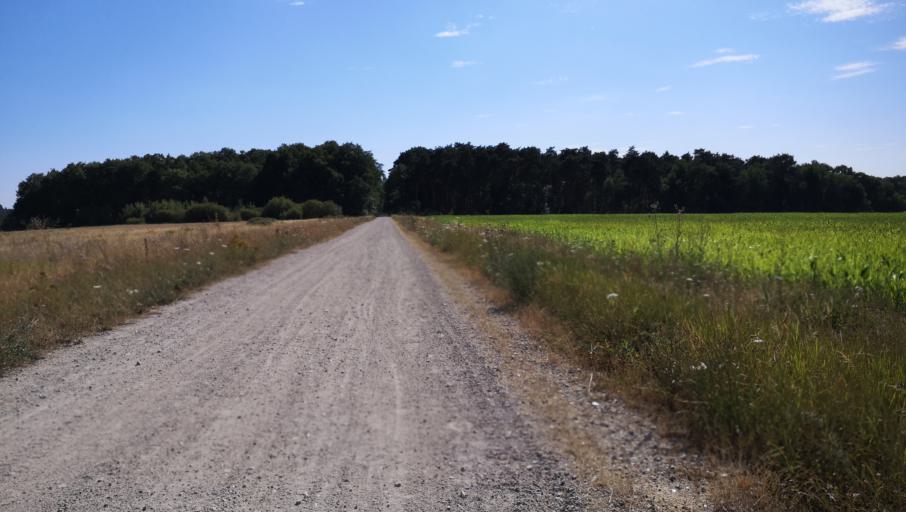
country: FR
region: Centre
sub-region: Departement du Loiret
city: Marigny-les-Usages
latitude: 47.9523
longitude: 2.0035
